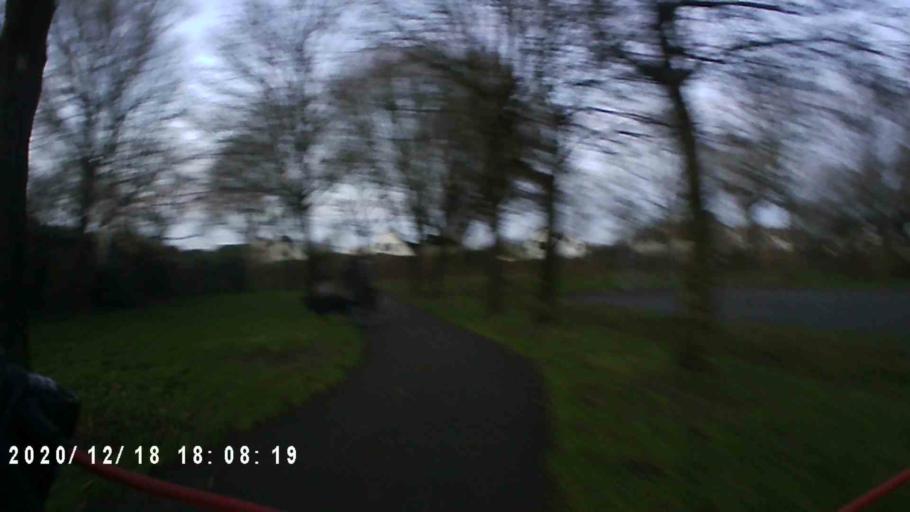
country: NL
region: Groningen
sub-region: Gemeente Haren
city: Haren
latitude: 53.1384
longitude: 6.5545
